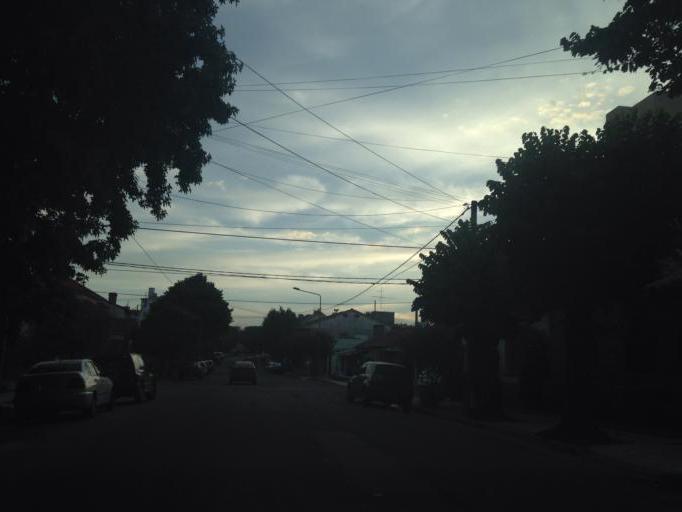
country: AR
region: Buenos Aires
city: Mar del Plata
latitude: -38.0176
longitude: -57.5459
